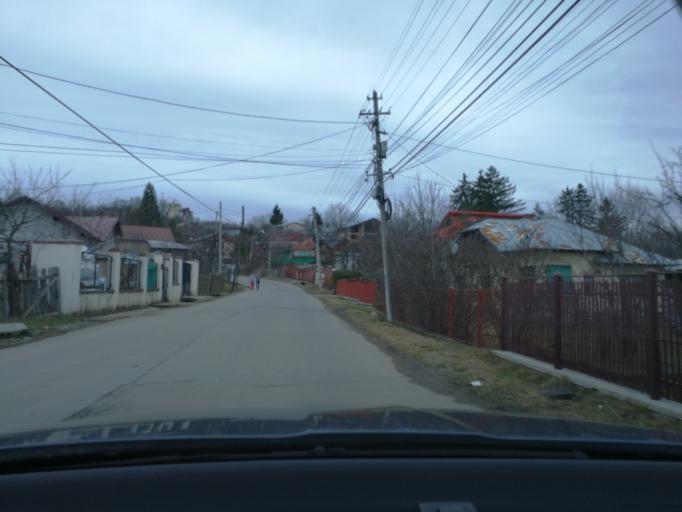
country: RO
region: Prahova
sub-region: Oras Breaza
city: Breaza
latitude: 45.1796
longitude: 25.6579
